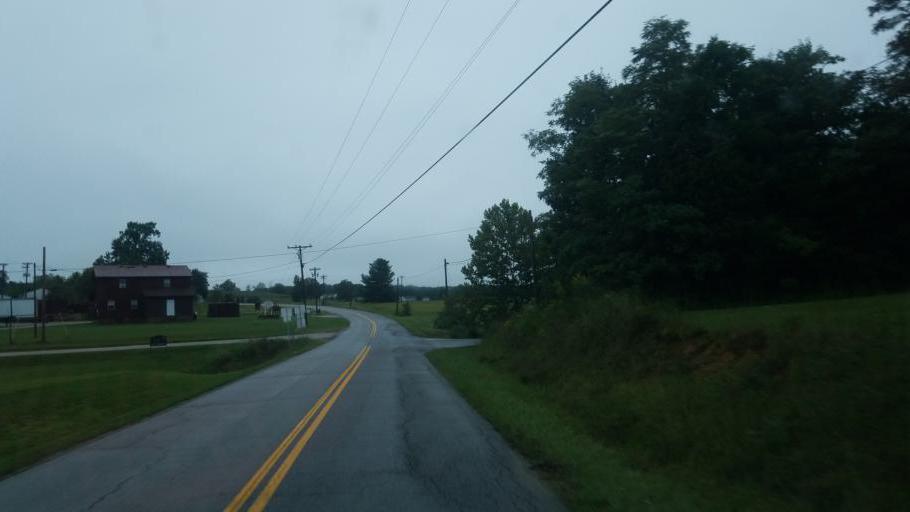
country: US
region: Kentucky
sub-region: Fleming County
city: Flemingsburg
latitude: 38.4062
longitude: -83.6422
